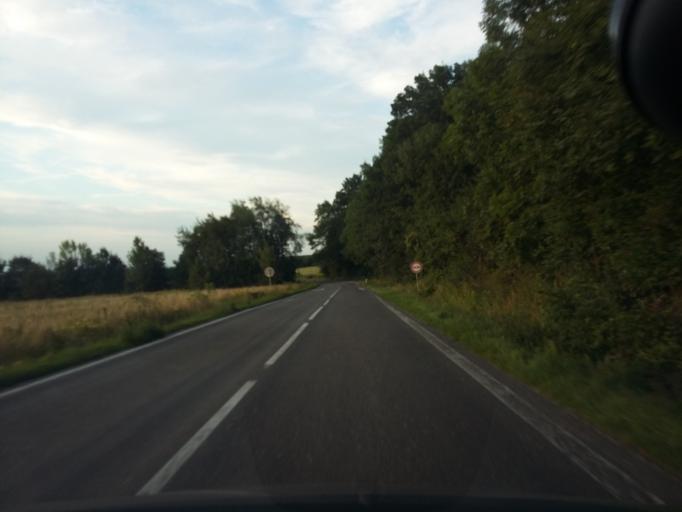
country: SK
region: Bratislavsky
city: Svaty Jur
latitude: 48.3723
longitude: 17.1481
